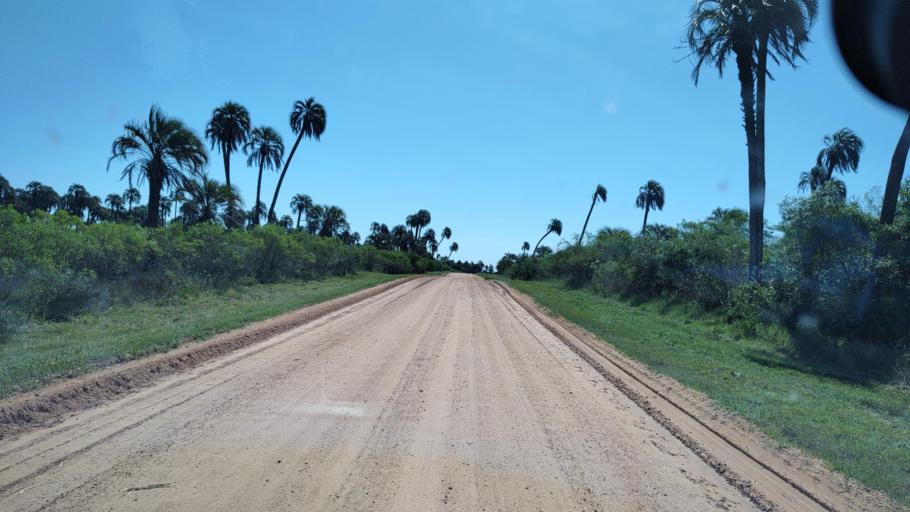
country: AR
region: Entre Rios
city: Ubajay
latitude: -31.8528
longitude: -58.2958
